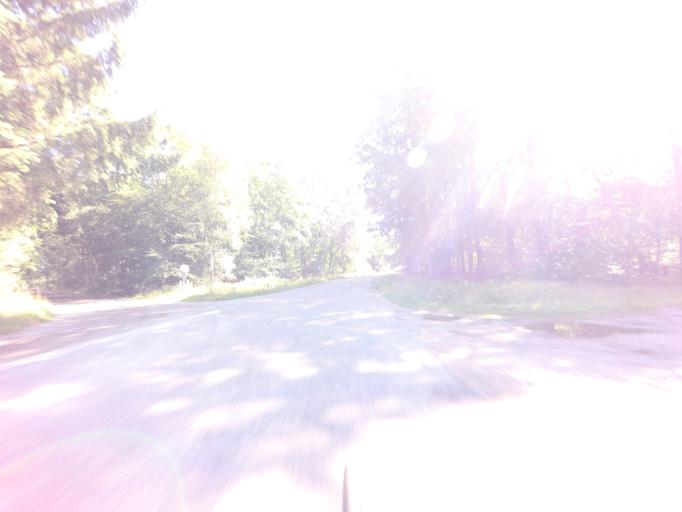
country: DK
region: North Denmark
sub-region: Hjorring Kommune
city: Hirtshals
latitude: 57.5821
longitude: 10.0027
